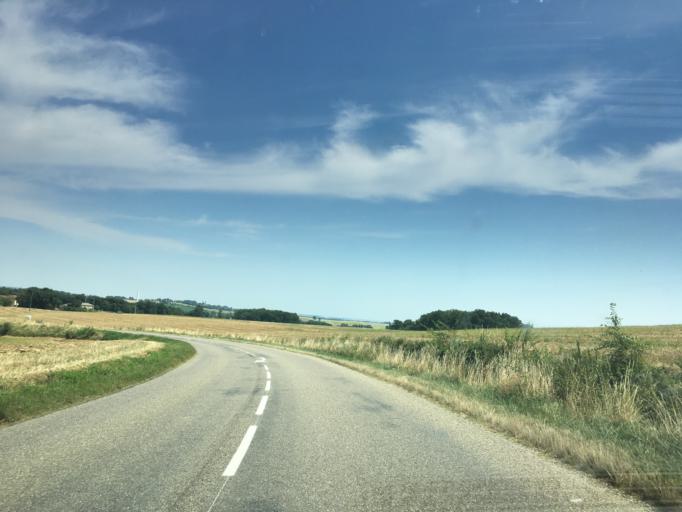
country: FR
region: Midi-Pyrenees
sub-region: Departement du Gers
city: Fleurance
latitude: 43.8621
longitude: 0.7313
